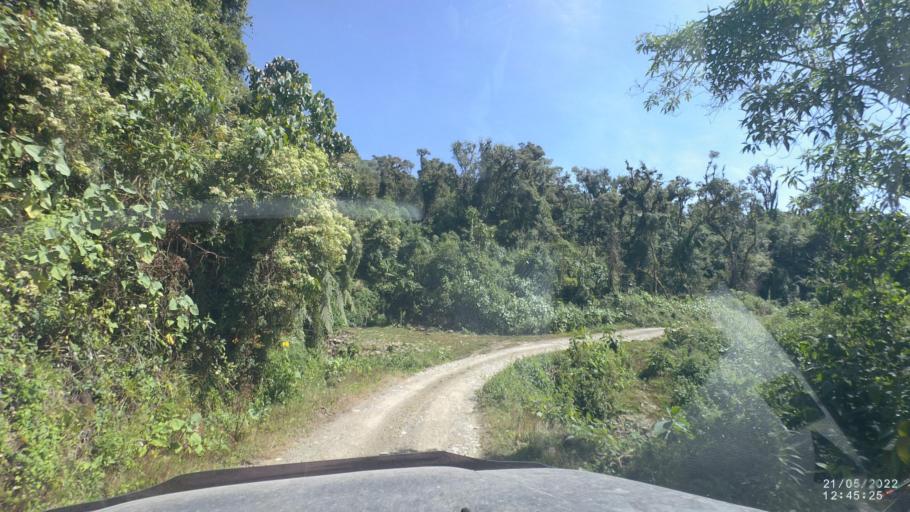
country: BO
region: Cochabamba
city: Colomi
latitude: -17.1879
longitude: -65.9357
